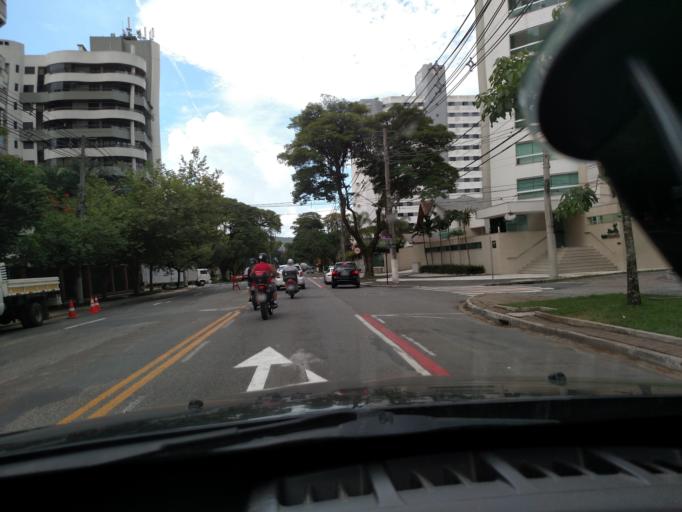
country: BR
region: Santa Catarina
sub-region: Blumenau
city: Blumenau
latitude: -26.9308
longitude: -49.0632
